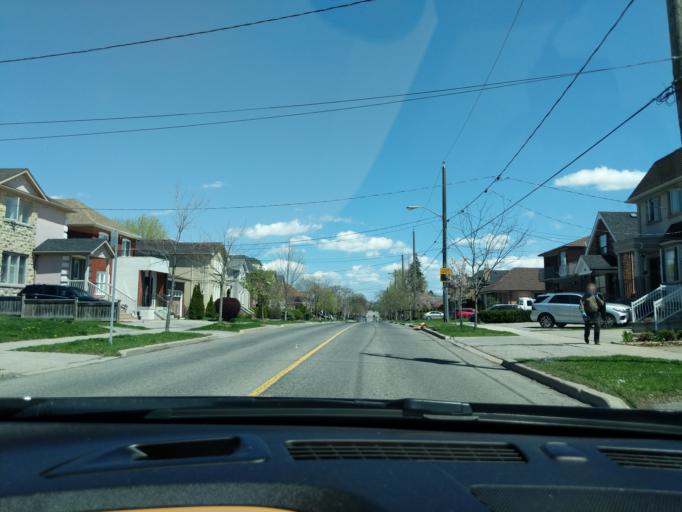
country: CA
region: Ontario
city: Toronto
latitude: 43.7103
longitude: -79.4378
